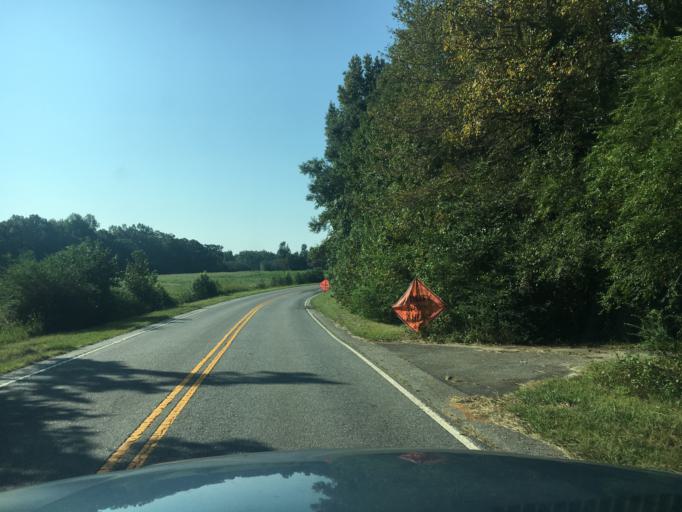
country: US
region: South Carolina
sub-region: Anderson County
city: Williamston
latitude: 34.6117
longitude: -82.3494
